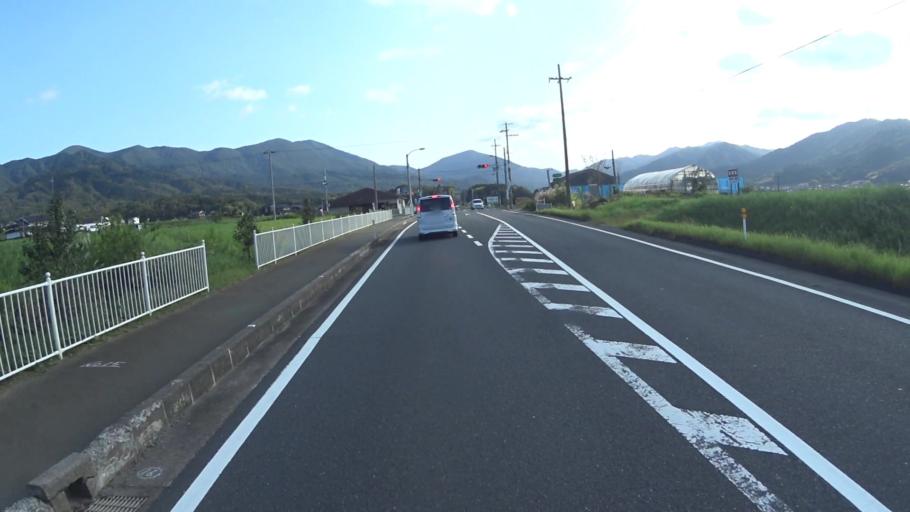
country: JP
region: Kyoto
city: Miyazu
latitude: 35.5046
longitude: 135.1038
